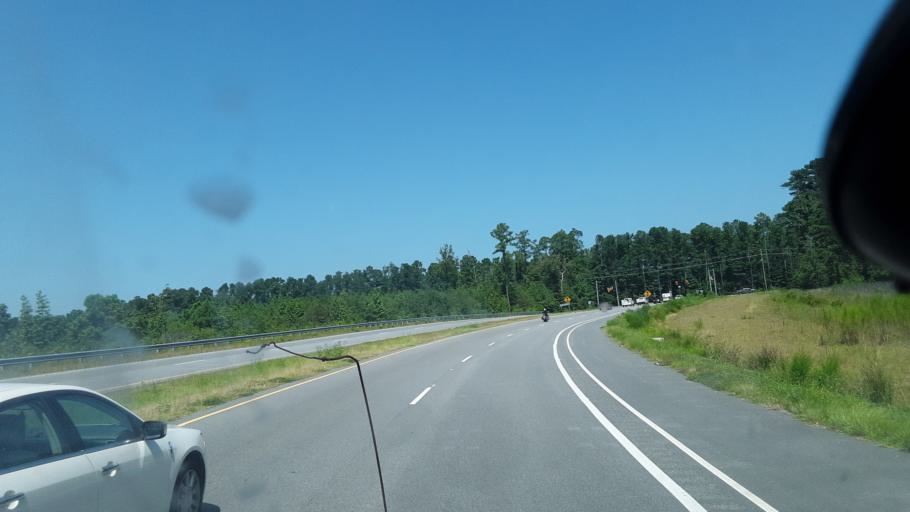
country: US
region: South Carolina
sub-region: Horry County
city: Red Hill
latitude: 33.8196
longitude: -78.9140
